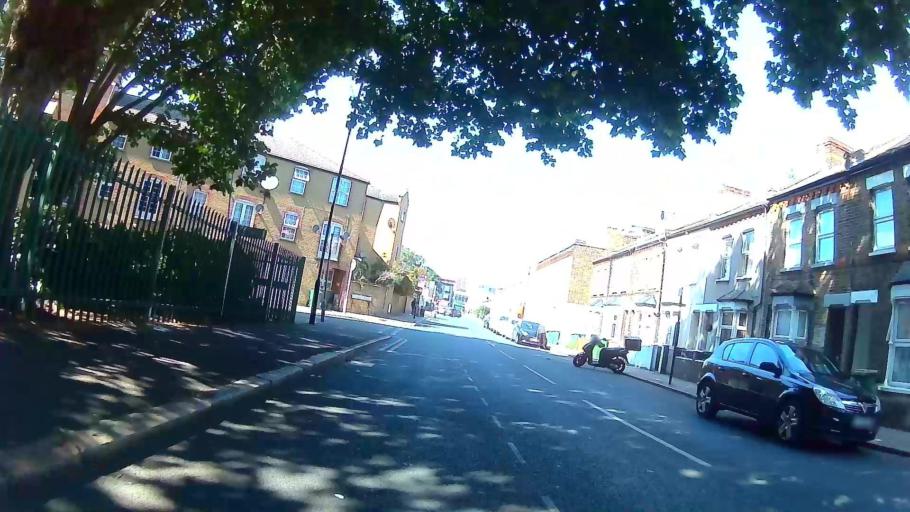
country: GB
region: England
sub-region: Greater London
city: East Ham
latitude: 51.5289
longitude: 0.0182
